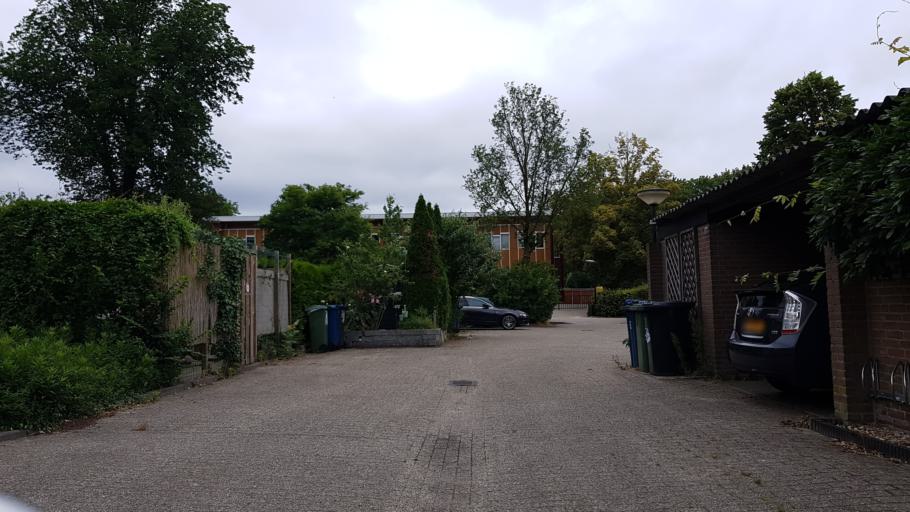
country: NL
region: Gelderland
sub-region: Gemeente Apeldoorn
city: Apeldoorn
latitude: 52.1973
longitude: 5.9866
